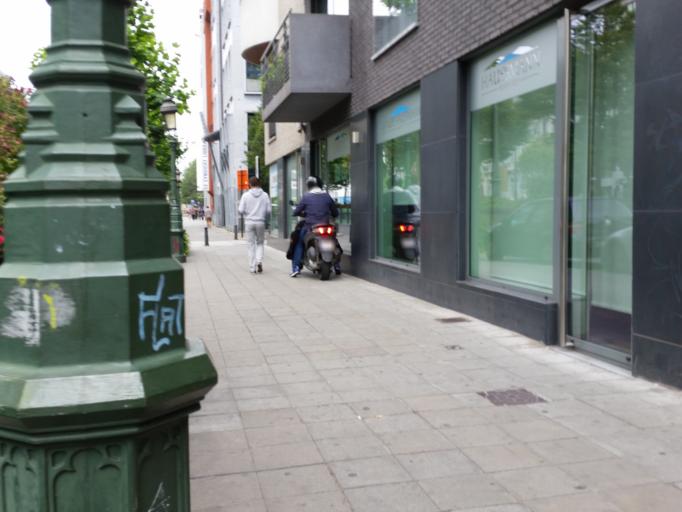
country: BE
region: Brussels Capital
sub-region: Bruxelles-Capitale
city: Brussels
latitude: 50.8573
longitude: 4.3518
